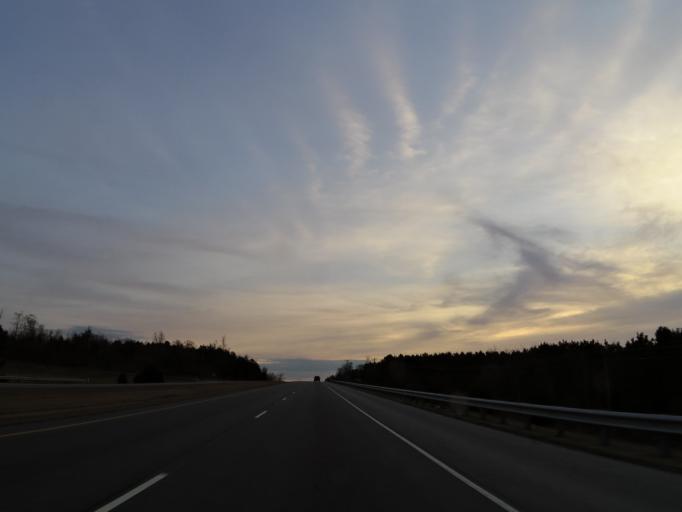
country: US
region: Tennessee
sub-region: McMinn County
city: Englewood
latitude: 35.3883
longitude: -84.5043
